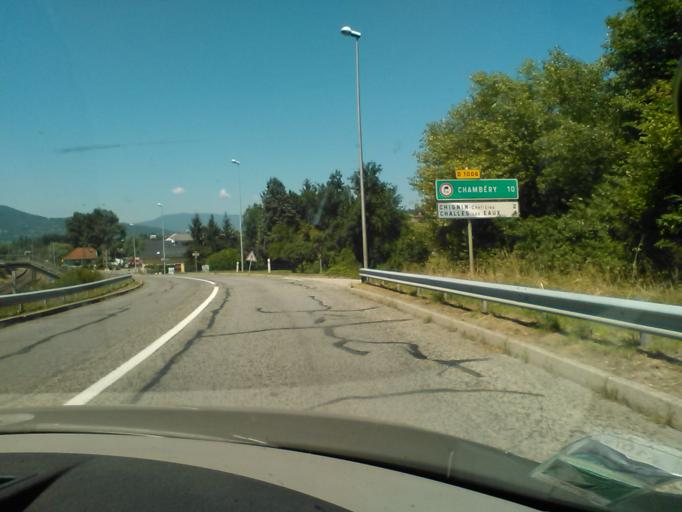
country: FR
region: Rhone-Alpes
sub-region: Departement de la Savoie
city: Les Marches
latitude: 45.5152
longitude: 6.0062
